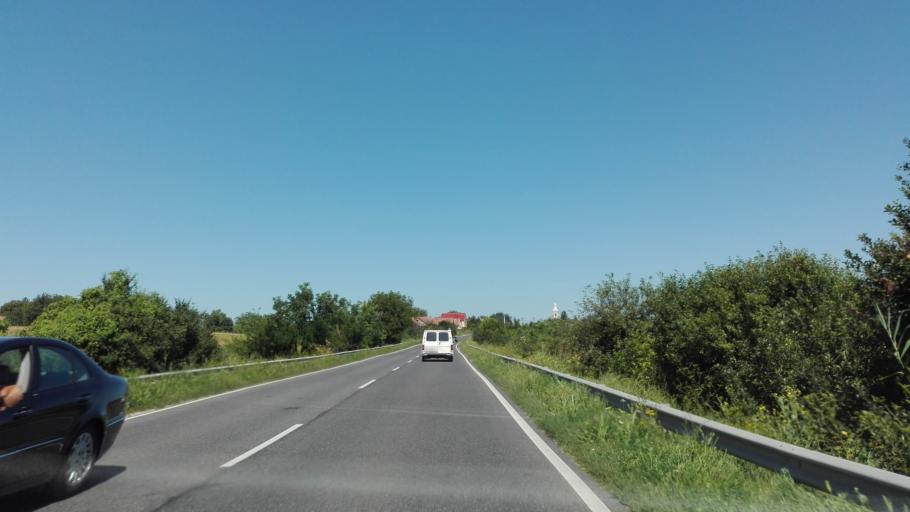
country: HU
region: Tolna
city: Simontornya
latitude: 46.7692
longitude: 18.5187
